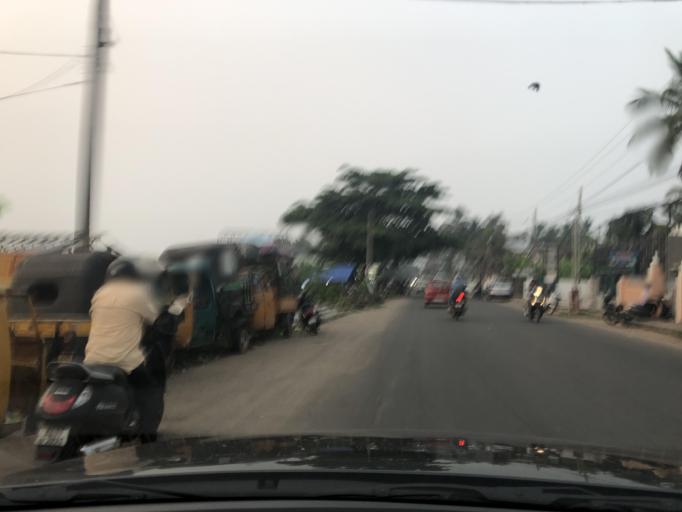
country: IN
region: Kerala
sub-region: Kozhikode
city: Kozhikode
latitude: 11.2399
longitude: 75.7747
